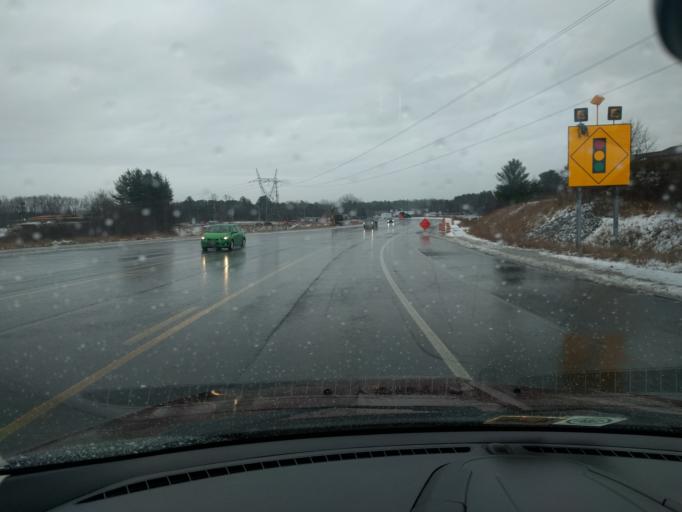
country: US
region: West Virginia
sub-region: Raleigh County
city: Stanaford
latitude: 37.8001
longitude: -81.1713
